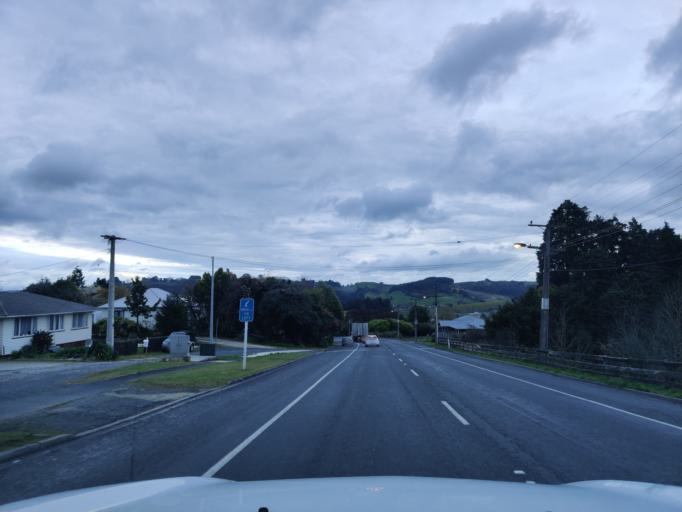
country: NZ
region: Waikato
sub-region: Otorohanga District
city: Otorohanga
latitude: -38.3471
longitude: 175.1679
